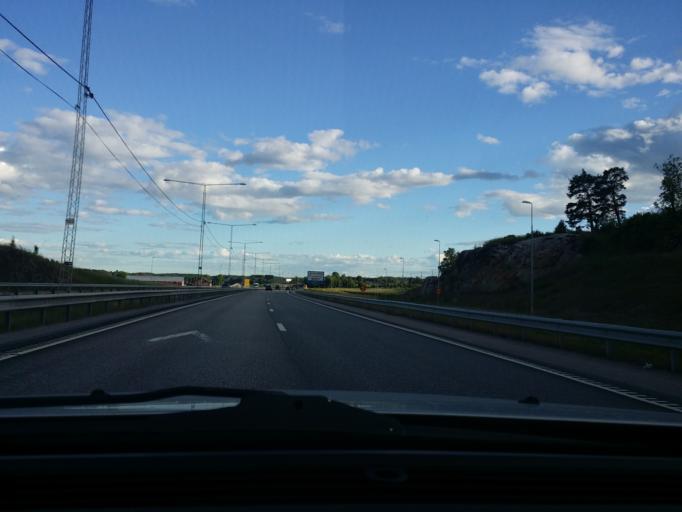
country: SE
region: Stockholm
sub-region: Sigtuna Kommun
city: Rosersberg
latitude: 59.5770
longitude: 17.9004
